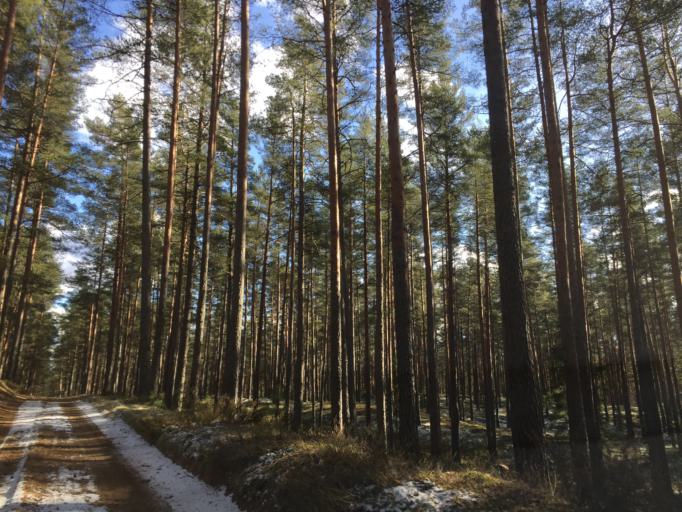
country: LV
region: Garkalne
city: Garkalne
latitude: 56.9638
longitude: 24.4516
